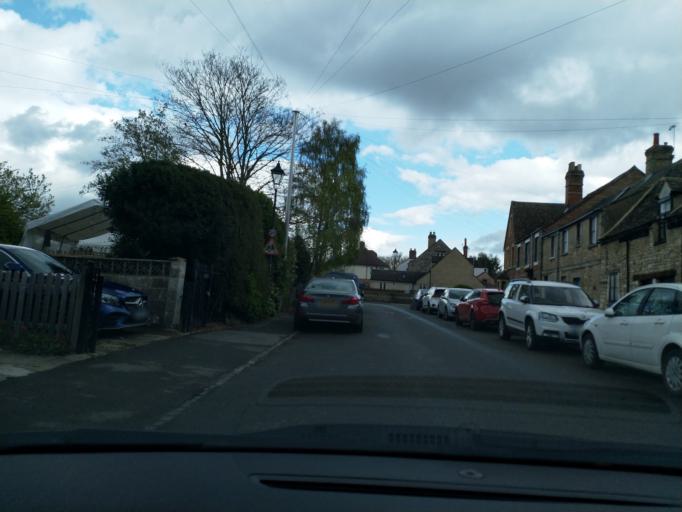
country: GB
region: England
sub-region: Oxfordshire
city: Yarnton
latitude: 51.7832
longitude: -1.2940
